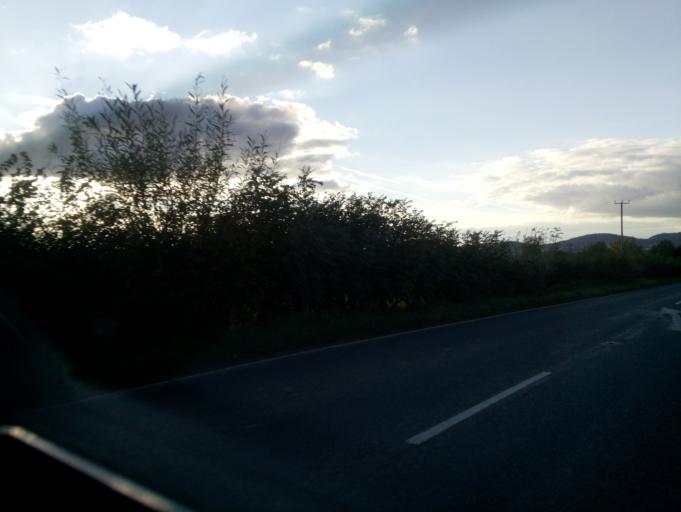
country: GB
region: England
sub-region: Worcestershire
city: Upton upon Severn
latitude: 52.0051
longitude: -2.2695
